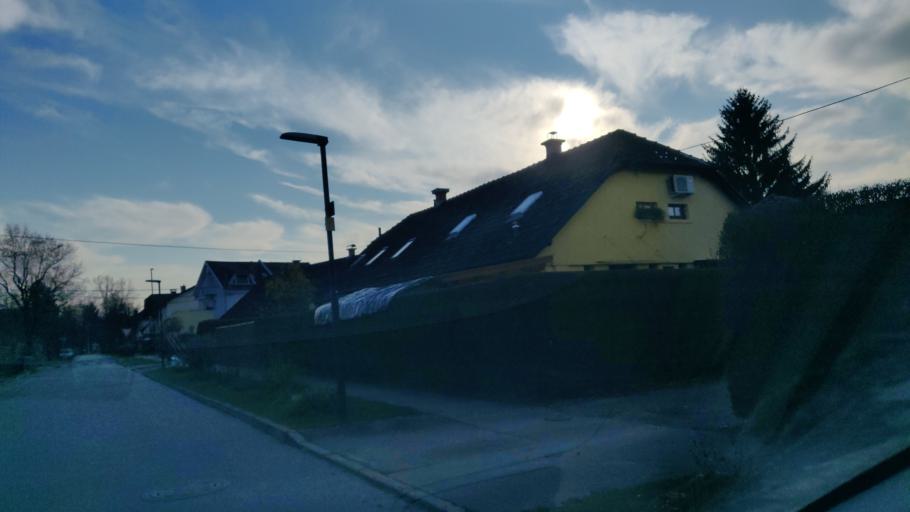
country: SI
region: Ljubljana
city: Ljubljana
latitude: 46.0415
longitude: 14.4950
